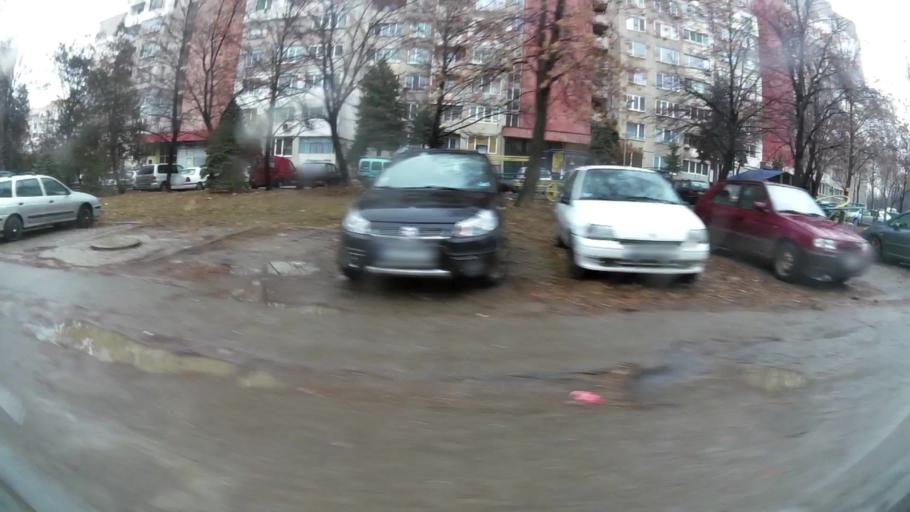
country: BG
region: Sofia-Capital
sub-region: Stolichna Obshtina
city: Sofia
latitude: 42.6405
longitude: 23.3680
